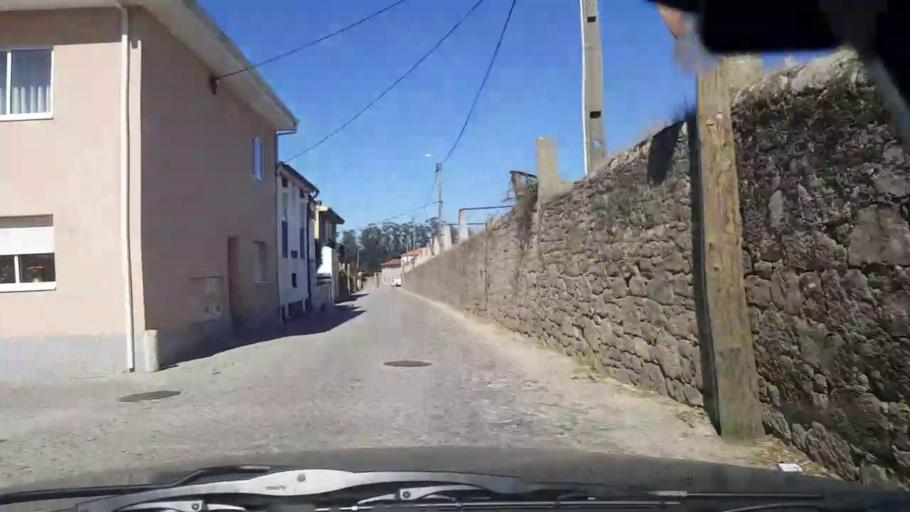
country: PT
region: Porto
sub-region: Vila do Conde
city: Arvore
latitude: 41.3254
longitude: -8.7050
